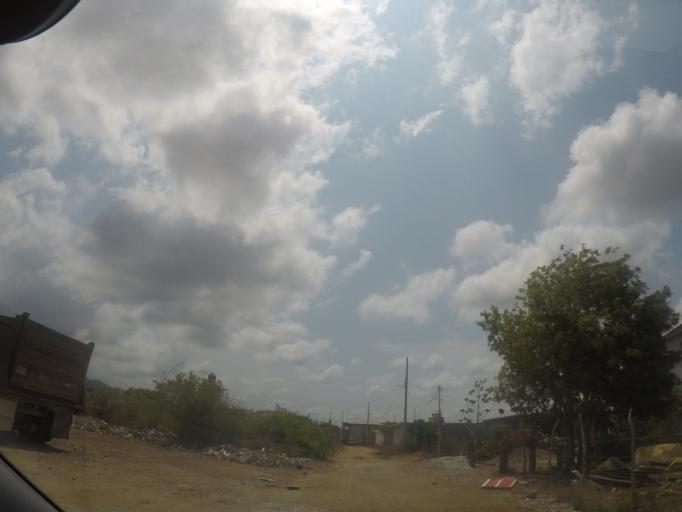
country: MX
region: Oaxaca
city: El Espinal
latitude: 16.5583
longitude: -94.9475
